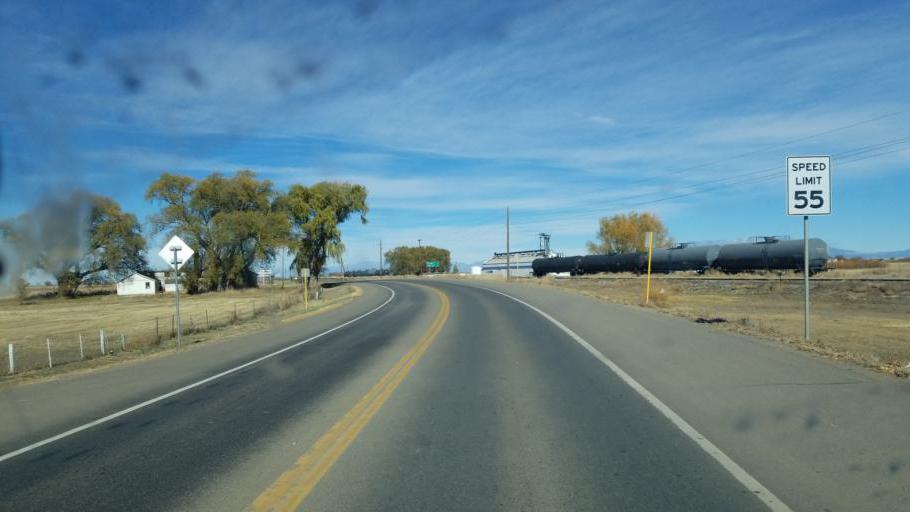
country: US
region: Colorado
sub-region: Conejos County
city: Conejos
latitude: 37.2793
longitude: -105.9601
